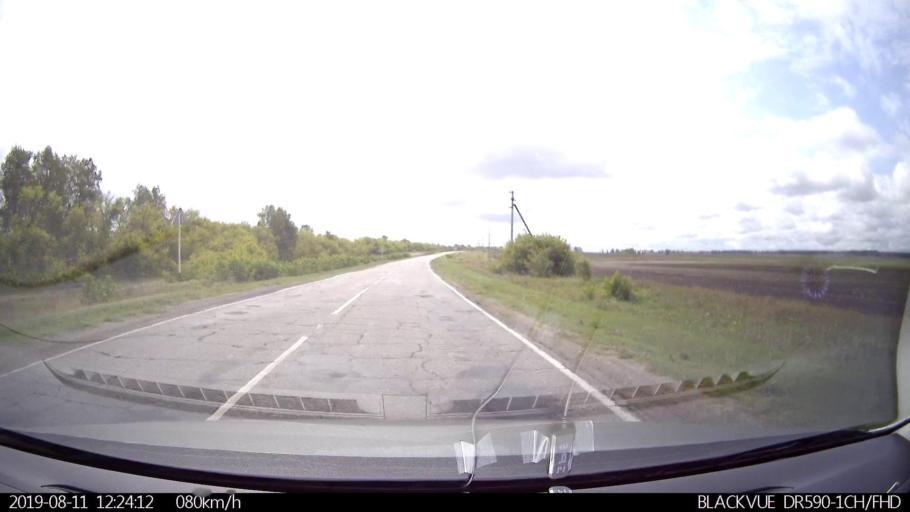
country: RU
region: Ulyanovsk
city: Ignatovka
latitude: 53.8860
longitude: 47.9498
